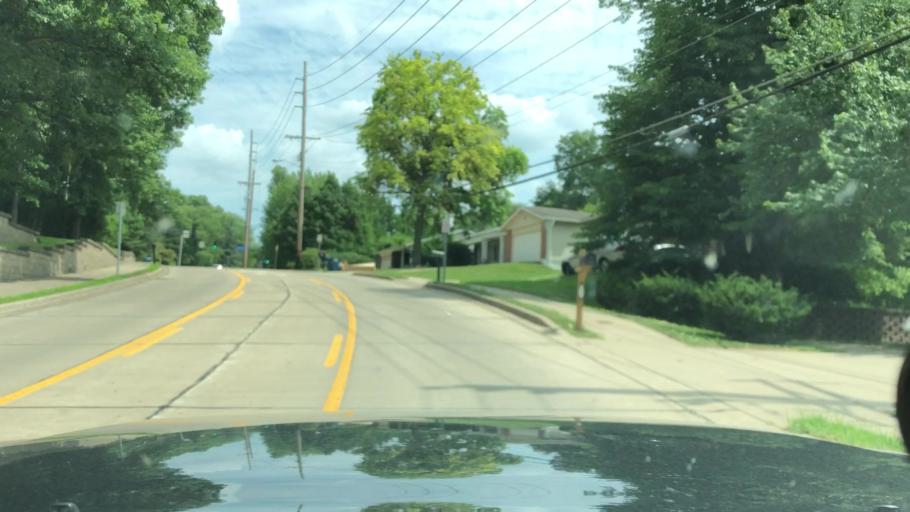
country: US
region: Missouri
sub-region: Saint Charles County
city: Saint Charles
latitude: 38.8071
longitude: -90.5104
